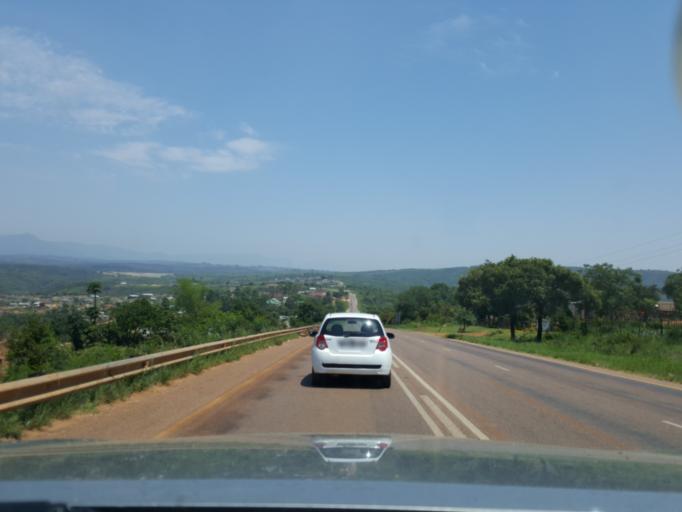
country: ZA
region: Limpopo
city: Thulamahashi
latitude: -24.9136
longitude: 31.1182
